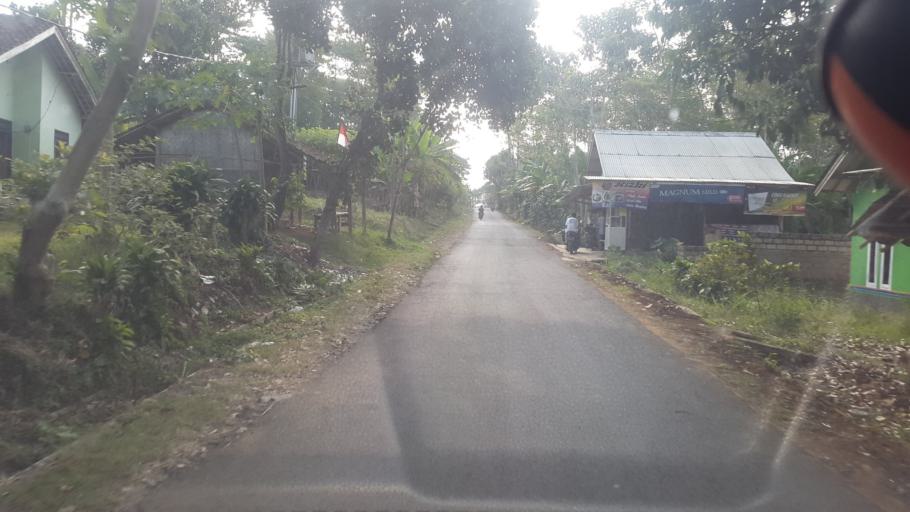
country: ID
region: West Java
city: Cicurug
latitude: -6.8471
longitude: 106.7390
